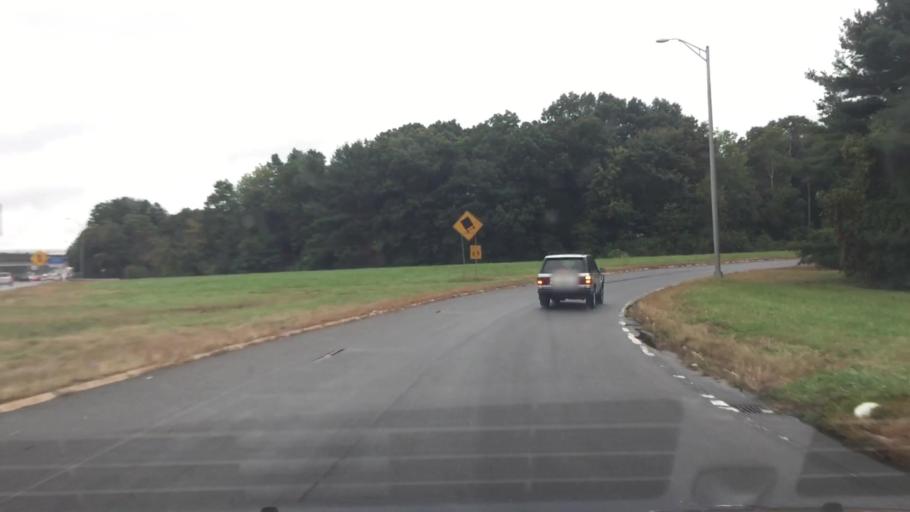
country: US
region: Massachusetts
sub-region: Essex County
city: Lawrence
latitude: 42.6690
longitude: -71.1968
